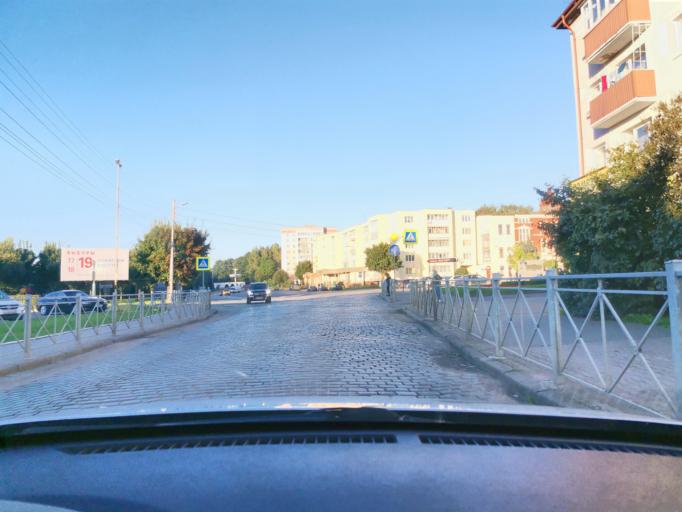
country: RU
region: Kaliningrad
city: Chernyakhovsk
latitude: 54.6370
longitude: 21.8081
